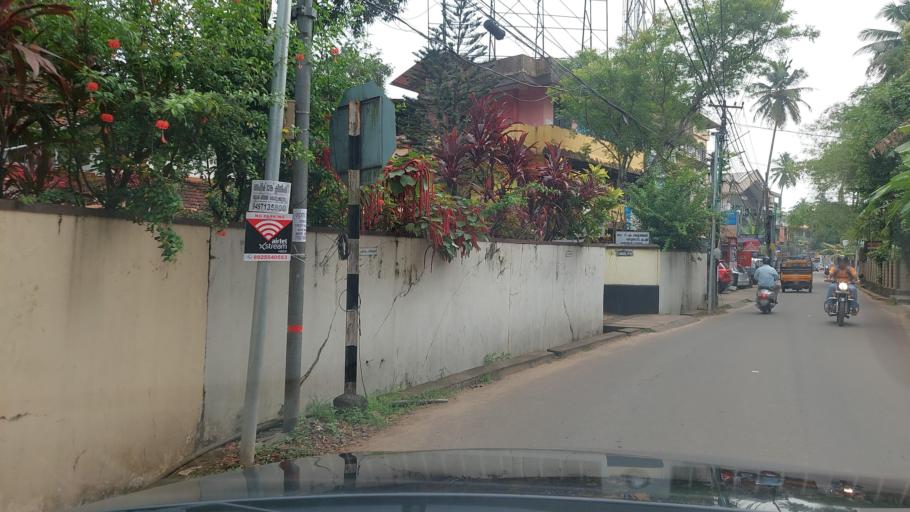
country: IN
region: Kerala
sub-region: Kozhikode
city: Kozhikode
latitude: 11.2516
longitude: 75.7880
